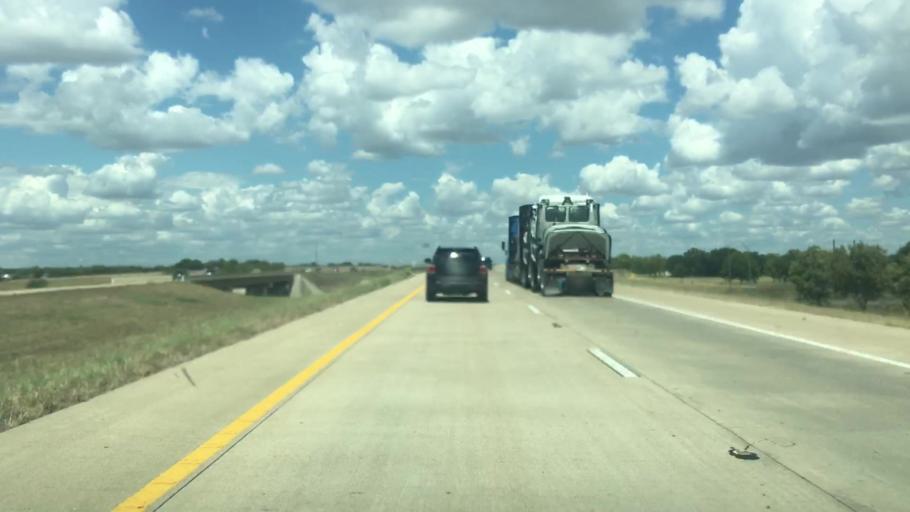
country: US
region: Texas
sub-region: Williamson County
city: Hutto
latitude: 30.5609
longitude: -97.5784
